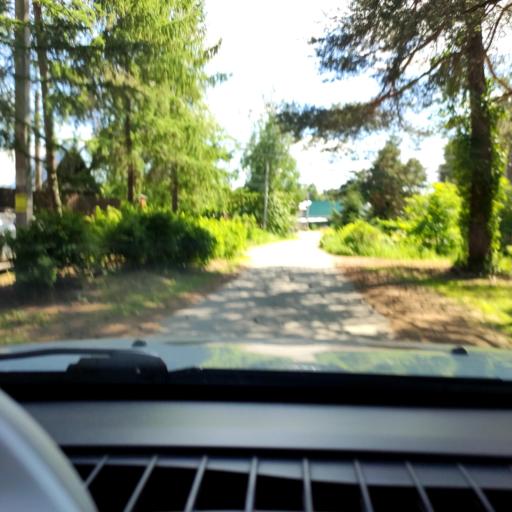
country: RU
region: Perm
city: Perm
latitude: 58.0592
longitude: 56.3071
